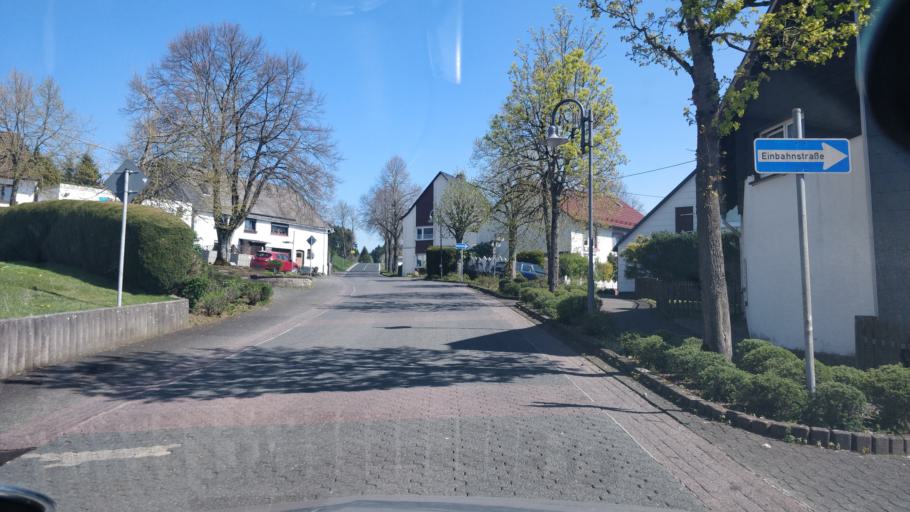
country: DE
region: Rheinland-Pfalz
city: Hellenhahn-Schellenberg
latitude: 50.6141
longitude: 8.0289
